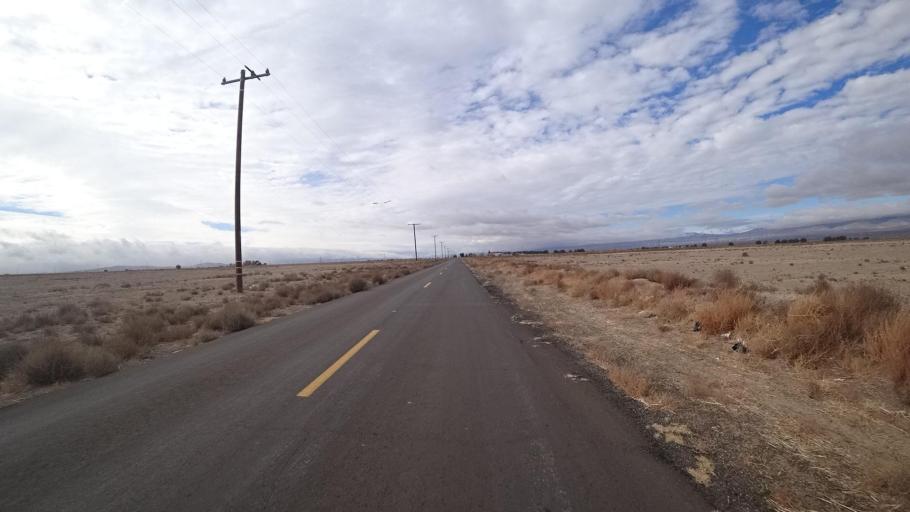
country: US
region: California
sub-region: Kern County
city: Rosamond
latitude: 34.8201
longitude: -118.2966
